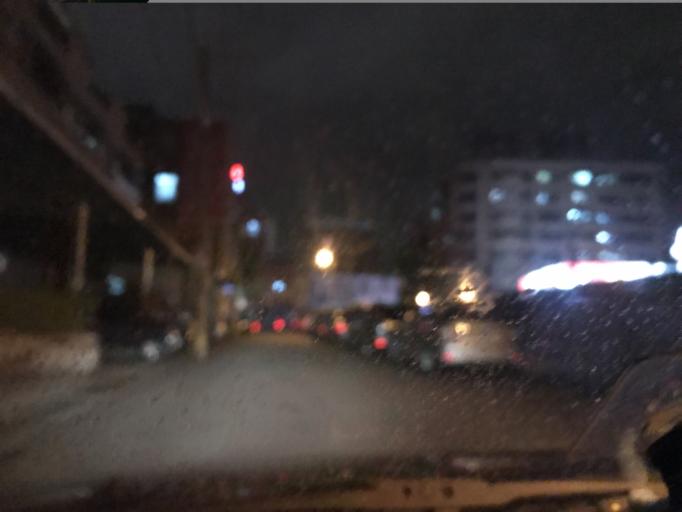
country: TW
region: Taiwan
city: Taoyuan City
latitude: 24.9459
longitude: 121.2449
